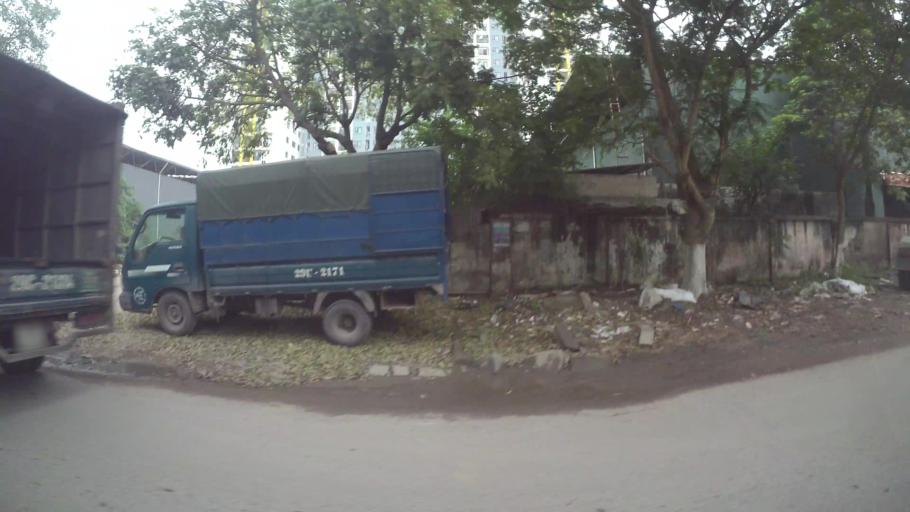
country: VN
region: Ha Noi
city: Hai BaTrung
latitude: 20.9828
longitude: 105.8709
